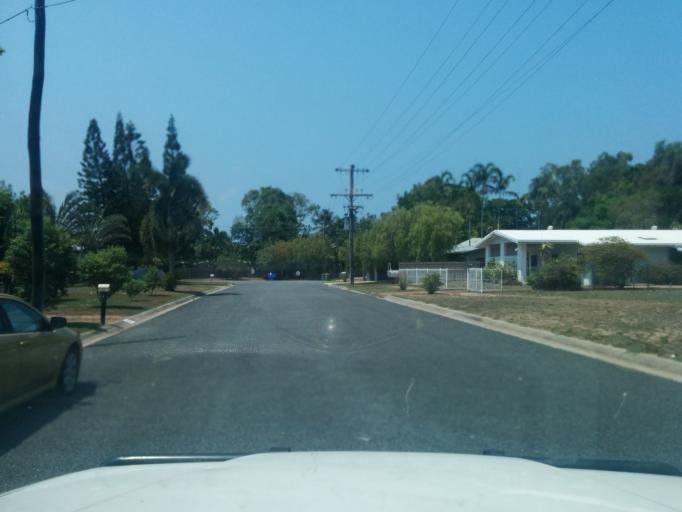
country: AU
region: Queensland
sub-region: Cairns
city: Redlynch
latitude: -16.8506
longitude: 145.7359
